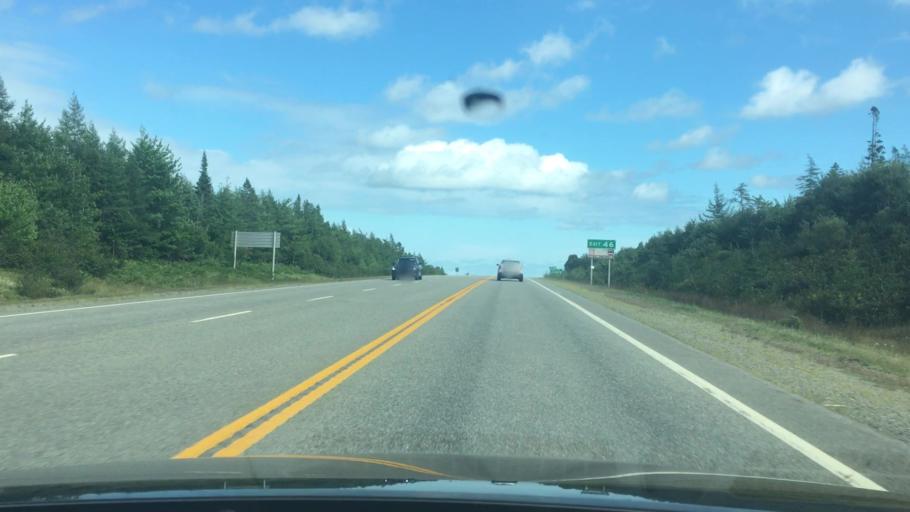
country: CA
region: Nova Scotia
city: Port Hawkesbury
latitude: 45.6148
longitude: -61.0936
